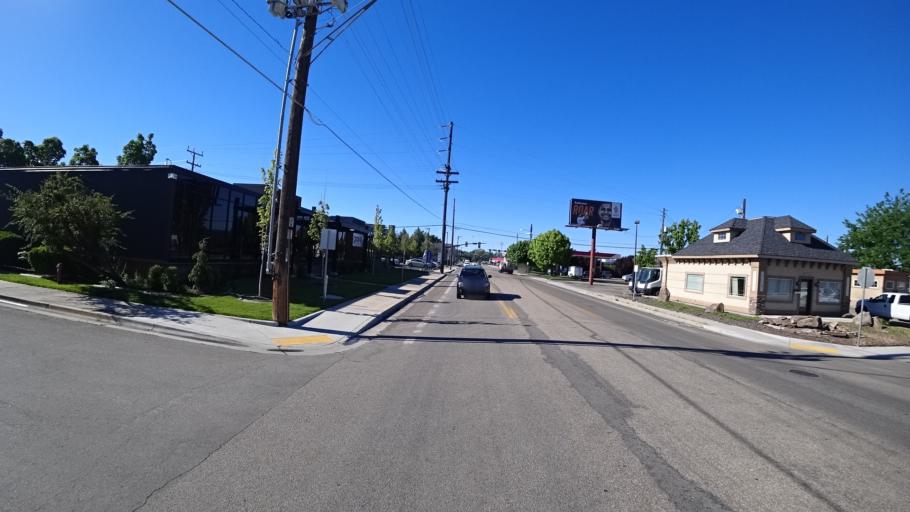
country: US
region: Idaho
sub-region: Ada County
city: Garden City
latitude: 43.6227
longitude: -116.2239
